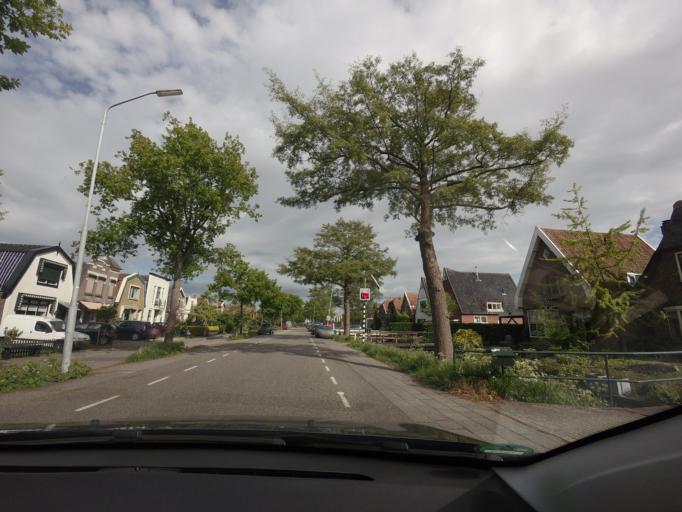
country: NL
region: North Holland
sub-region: Gemeente Beemster
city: Halfweg
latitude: 52.5141
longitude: 4.9399
